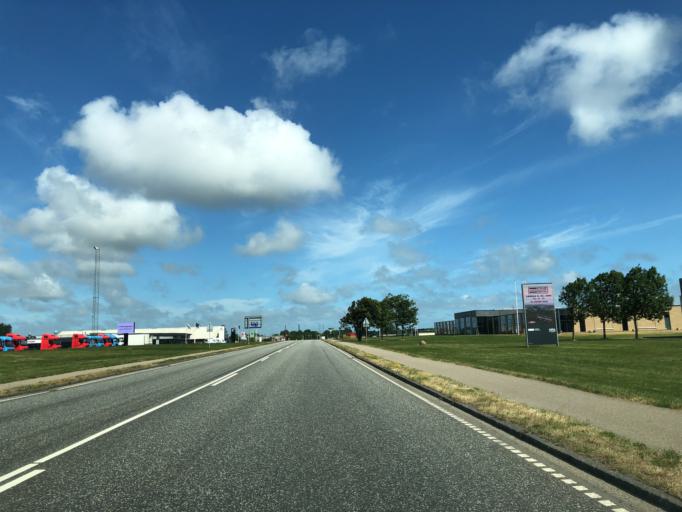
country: DK
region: Central Jutland
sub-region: Struer Kommune
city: Struer
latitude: 56.4731
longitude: 8.5860
